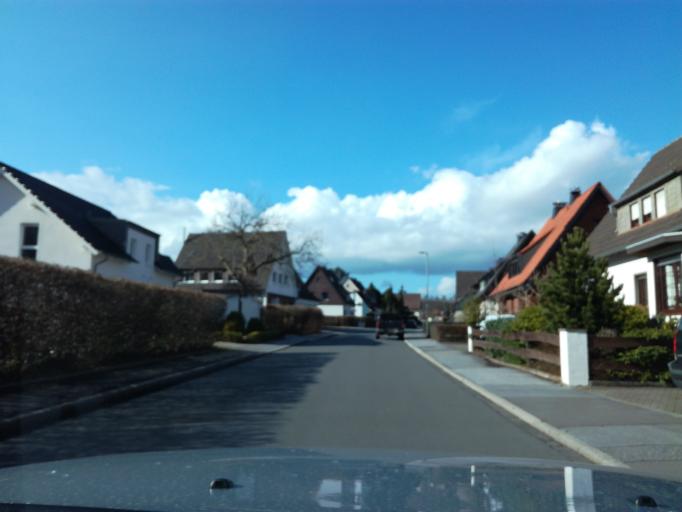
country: DE
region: North Rhine-Westphalia
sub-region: Regierungsbezirk Arnsberg
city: Menden
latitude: 51.4337
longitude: 7.7577
